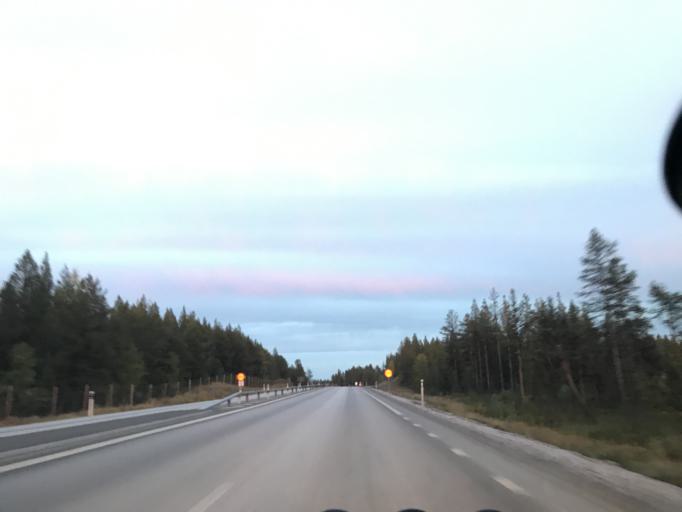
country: SE
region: Norrbotten
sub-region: Gallivare Kommun
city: Malmberget
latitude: 67.6691
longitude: 20.9564
